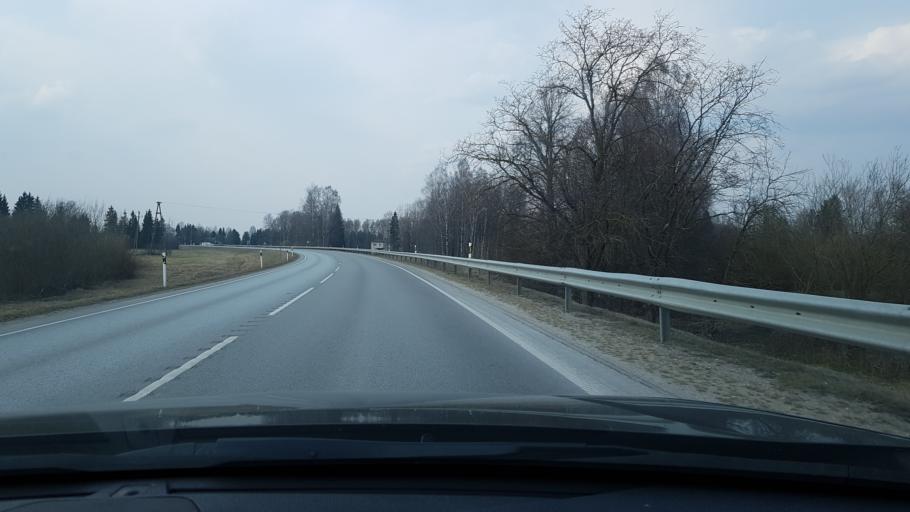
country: EE
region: Tartu
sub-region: Tartu linn
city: Tartu
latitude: 58.4019
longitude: 26.6815
